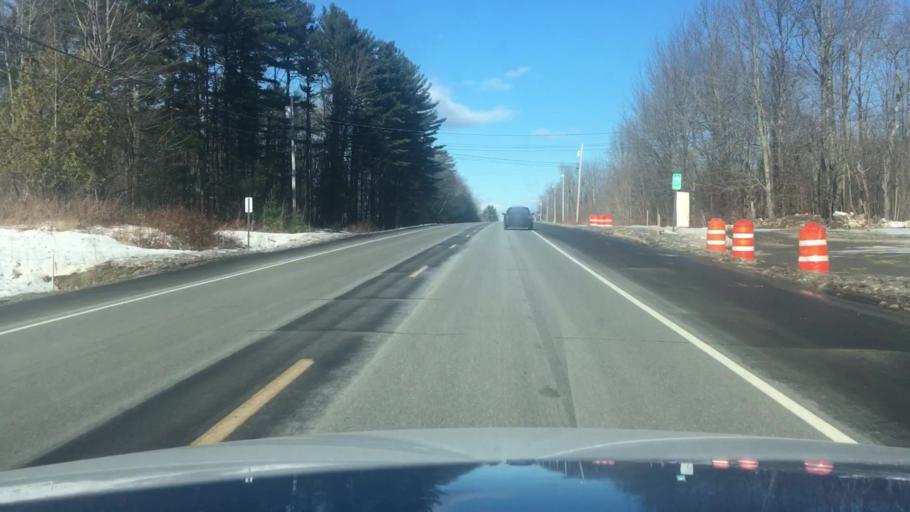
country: US
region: Maine
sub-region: Kennebec County
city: Waterville
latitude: 44.6201
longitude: -69.6714
